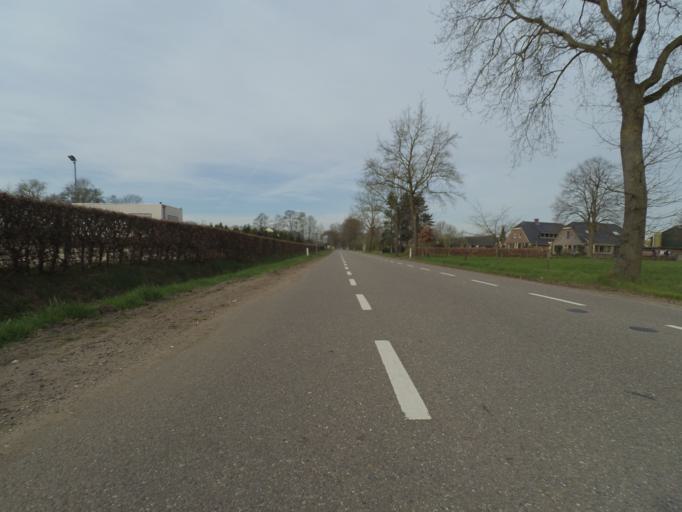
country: NL
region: Gelderland
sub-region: Gemeente Ede
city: Lunteren
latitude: 52.0716
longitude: 5.6307
